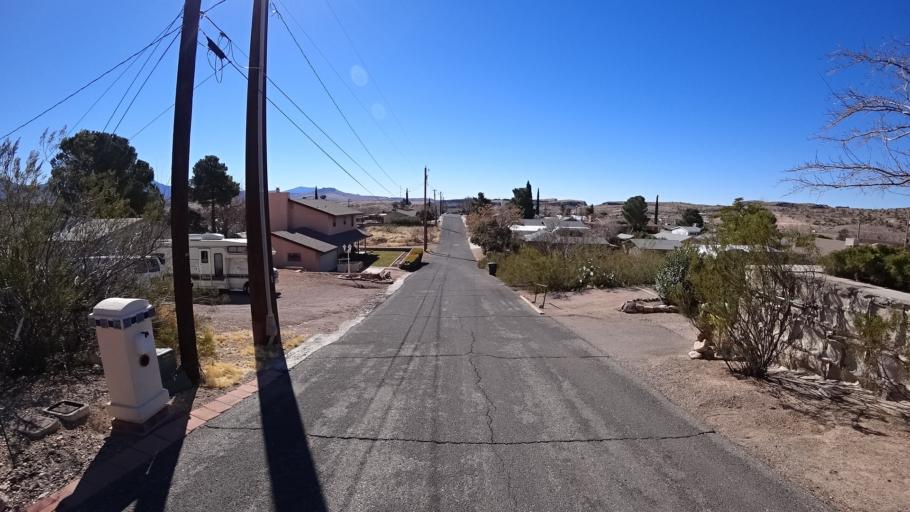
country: US
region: Arizona
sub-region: Mohave County
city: Kingman
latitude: 35.1991
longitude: -114.0630
